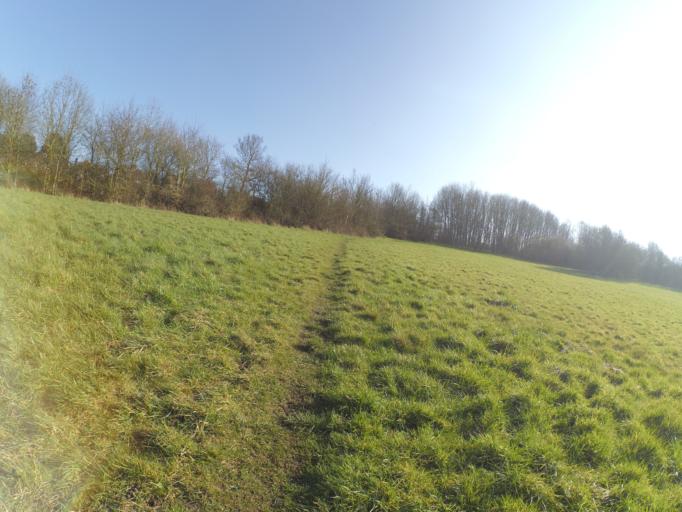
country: GB
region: England
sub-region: Greater London
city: Wembley
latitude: 51.5754
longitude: -0.2700
